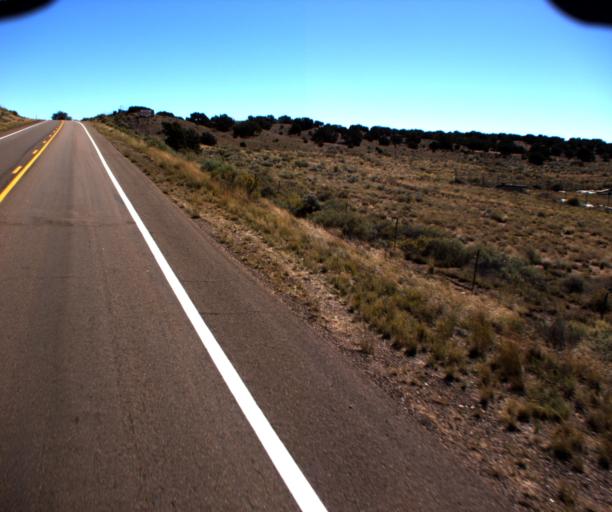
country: US
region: Arizona
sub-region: Apache County
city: Saint Johns
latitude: 34.5063
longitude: -109.4162
